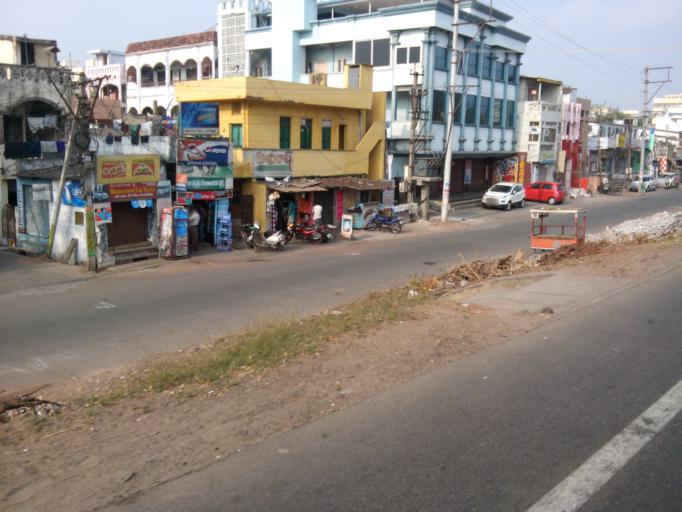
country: IN
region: Andhra Pradesh
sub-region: Krishna
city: Vijayawada
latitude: 16.5070
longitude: 80.6255
